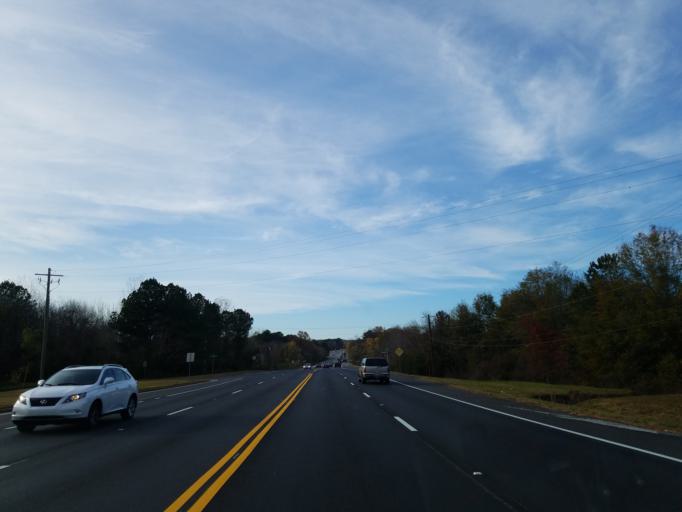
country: US
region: Georgia
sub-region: Cobb County
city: Mableton
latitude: 33.7774
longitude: -84.5305
